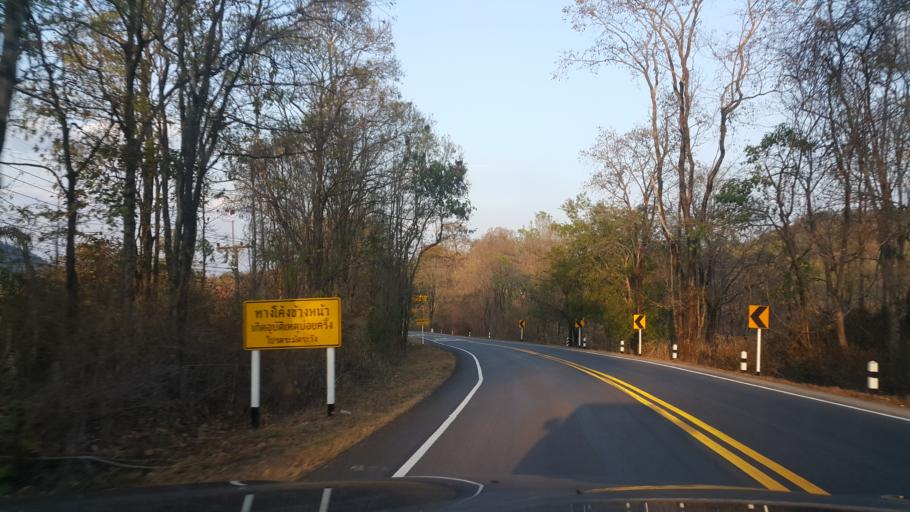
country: TH
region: Loei
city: Phu Ruea
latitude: 17.4608
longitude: 101.5313
